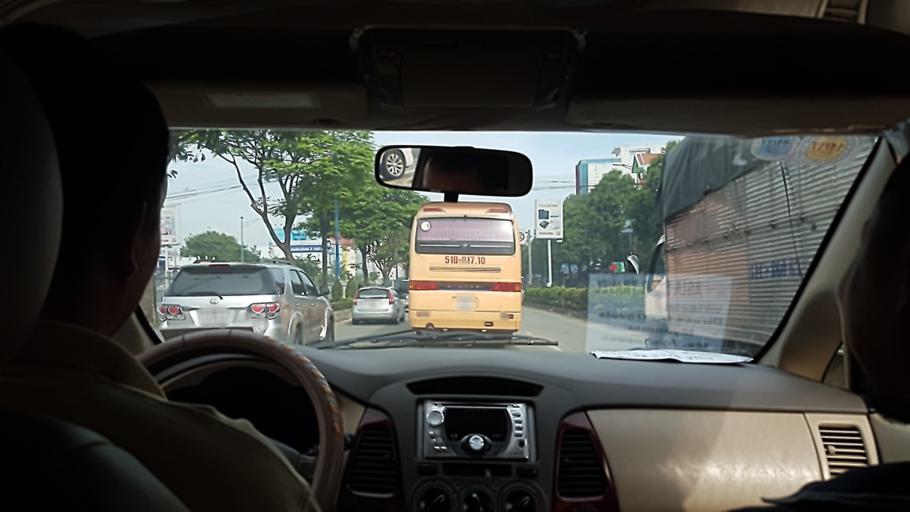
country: VN
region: Ho Chi Minh City
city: Ho Chi Minh City
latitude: 10.8312
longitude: 106.6227
